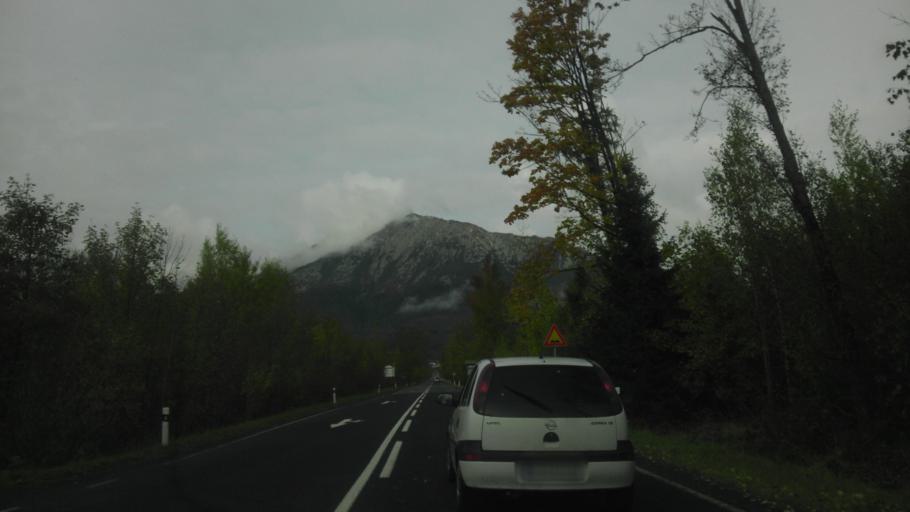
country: SK
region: Presovsky
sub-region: Okres Poprad
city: Vysoke Tatry
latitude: 49.1241
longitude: 20.2459
